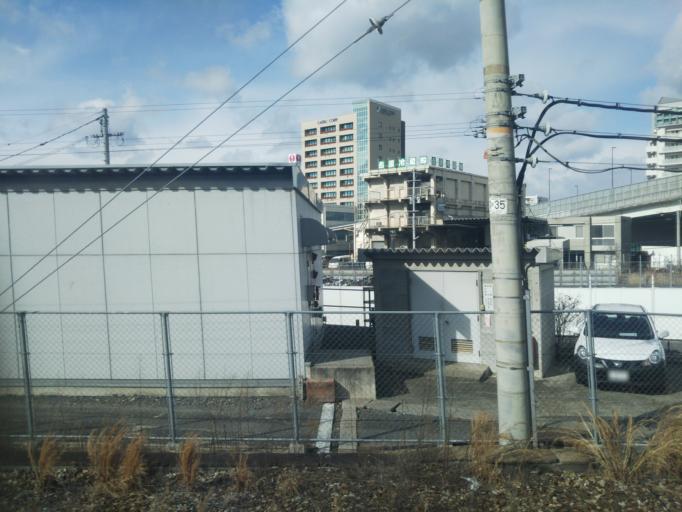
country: JP
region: Okayama
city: Okayama-shi
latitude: 34.6634
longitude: 133.9152
